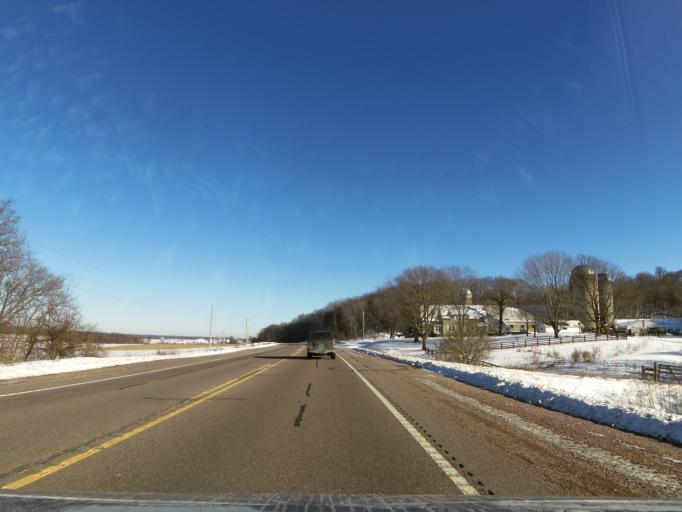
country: US
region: Wisconsin
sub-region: Columbia County
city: Lake Wisconsin
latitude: 43.5035
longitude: -89.6093
